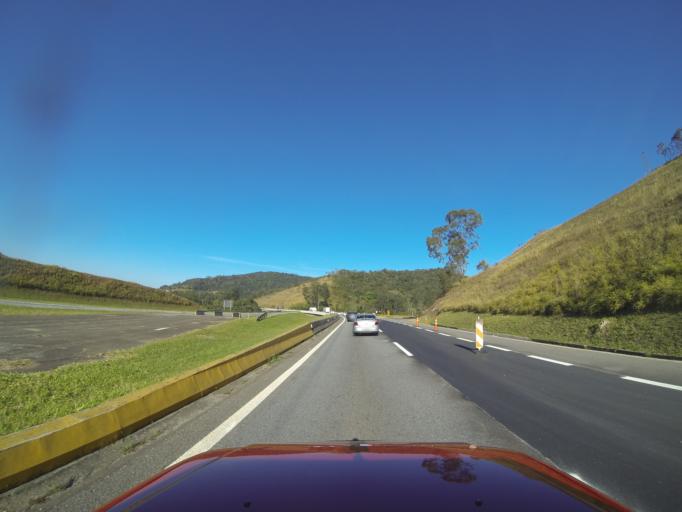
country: BR
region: Sao Paulo
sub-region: Bom Jesus Dos Perdoes
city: Bom Jesus dos Perdoes
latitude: -23.1935
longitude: -46.3489
